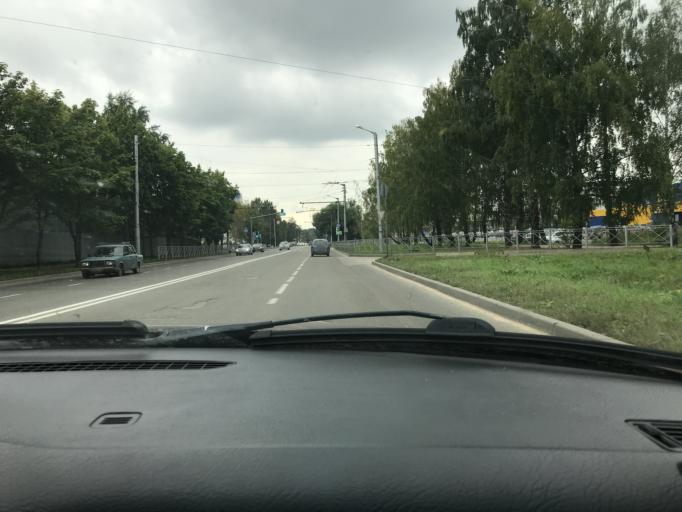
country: RU
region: Kaluga
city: Kaluga
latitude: 54.5408
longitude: 36.3164
